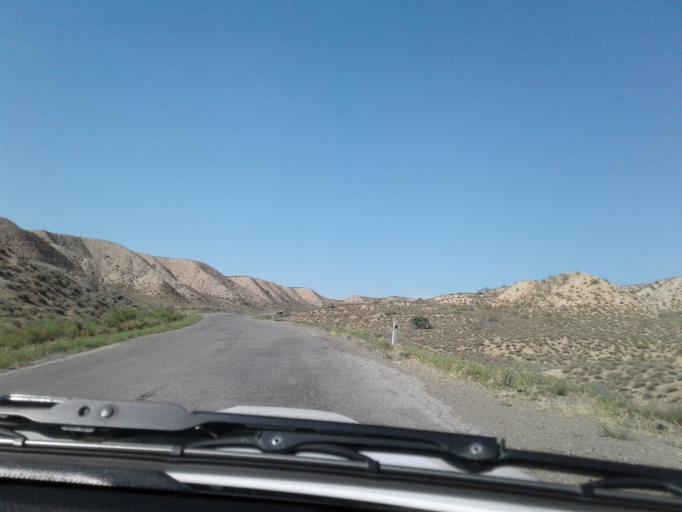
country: TM
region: Balkan
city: Magtymguly
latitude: 38.6516
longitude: 56.2763
